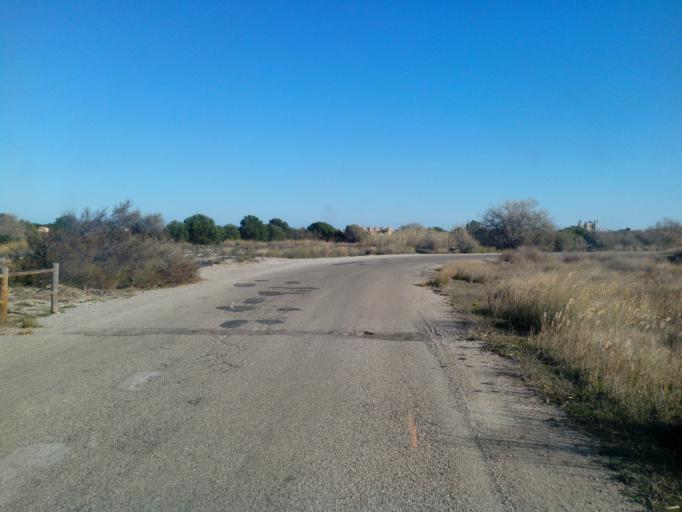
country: FR
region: Languedoc-Roussillon
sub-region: Departement des Pyrenees-Orientales
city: Le Barcares
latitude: 42.8400
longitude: 3.0294
